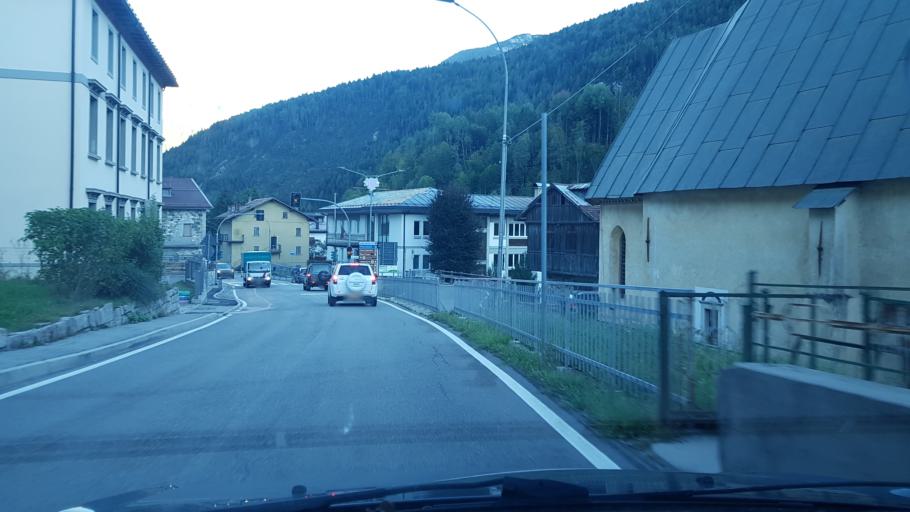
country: IT
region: Veneto
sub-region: Provincia di Belluno
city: Forno di Zoldo
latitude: 46.3464
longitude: 12.1704
